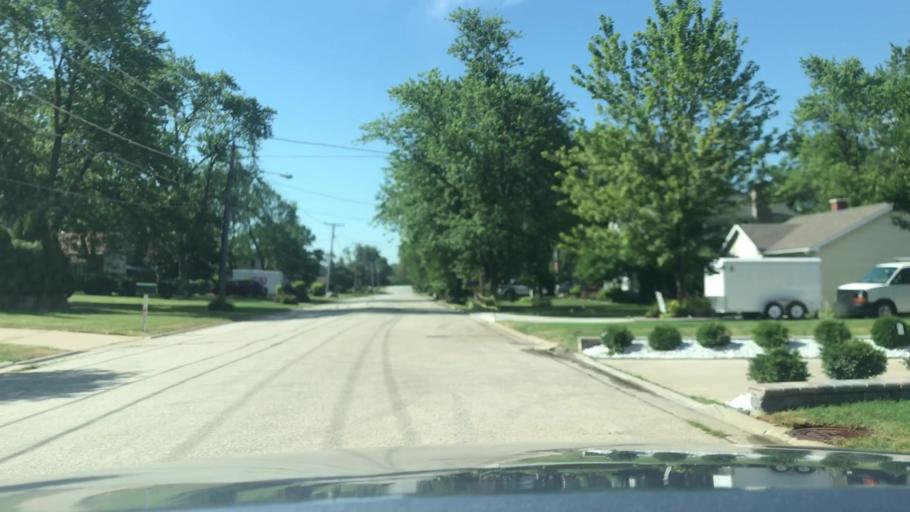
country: US
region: Illinois
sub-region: Cook County
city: Justice
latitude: 41.7391
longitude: -87.8302
